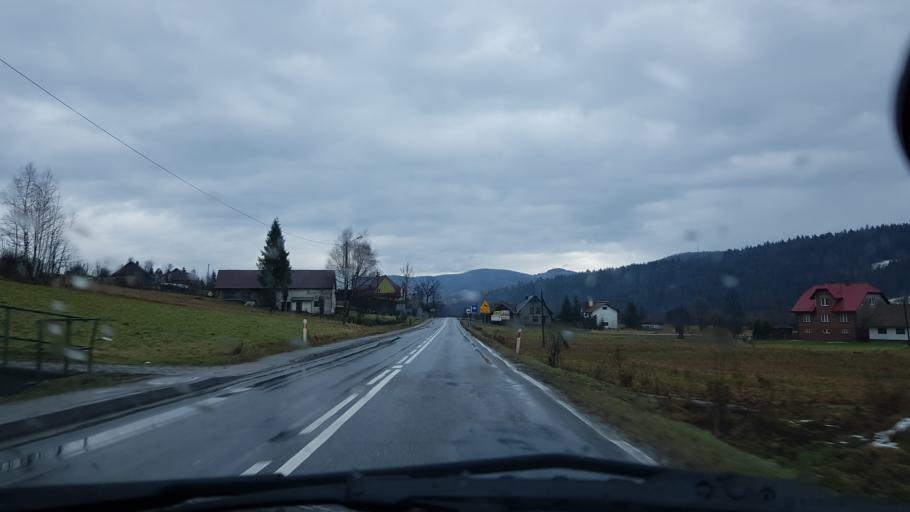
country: PL
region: Lesser Poland Voivodeship
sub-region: Powiat suski
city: Kukow
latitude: 49.7331
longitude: 19.4820
